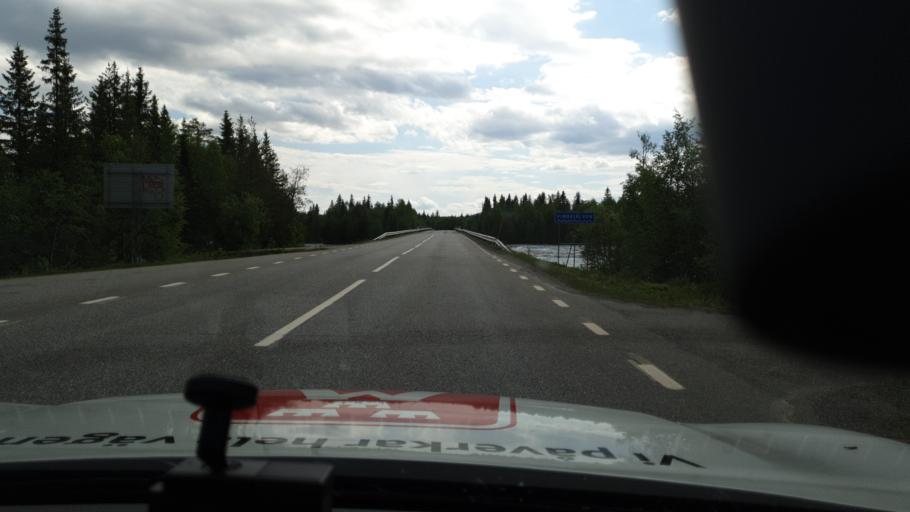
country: SE
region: Vaesterbotten
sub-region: Sorsele Kommun
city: Sorsele
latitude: 65.3112
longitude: 17.6548
